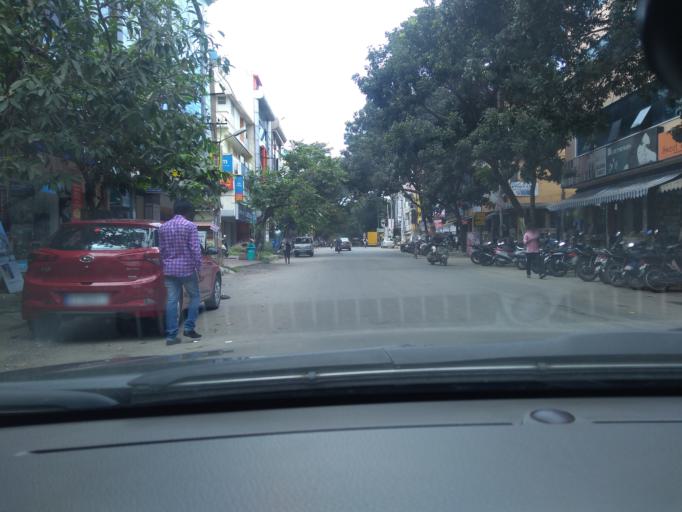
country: IN
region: Karnataka
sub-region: Bangalore Urban
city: Bangalore
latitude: 13.0014
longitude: 77.6617
